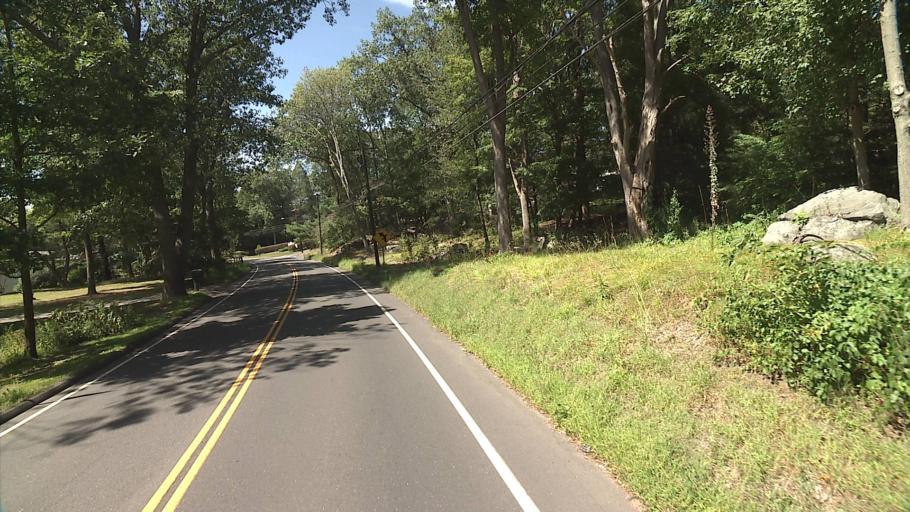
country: US
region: Connecticut
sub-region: New Haven County
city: Middlebury
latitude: 41.5267
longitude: -73.0899
